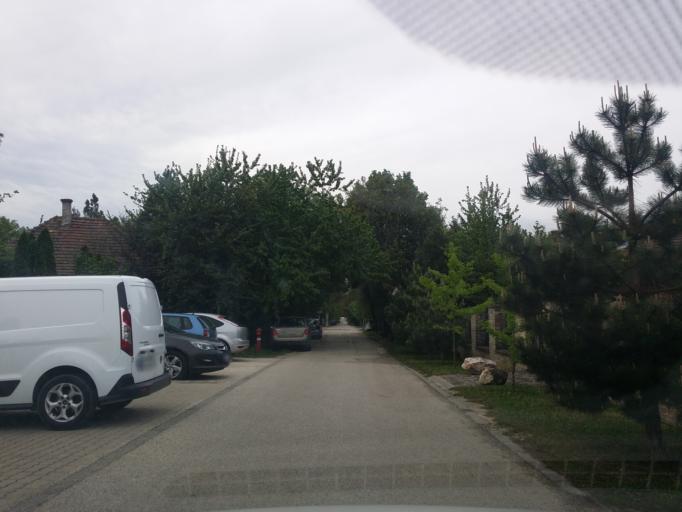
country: HU
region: Pest
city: Biatorbagy
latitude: 47.4803
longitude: 18.8200
